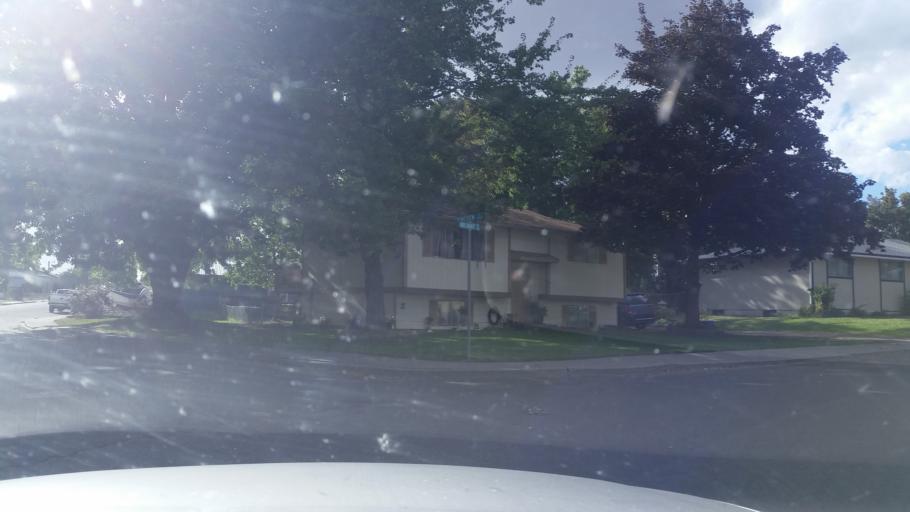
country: US
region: Washington
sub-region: Spokane County
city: Cheney
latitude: 47.4789
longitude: -117.5983
